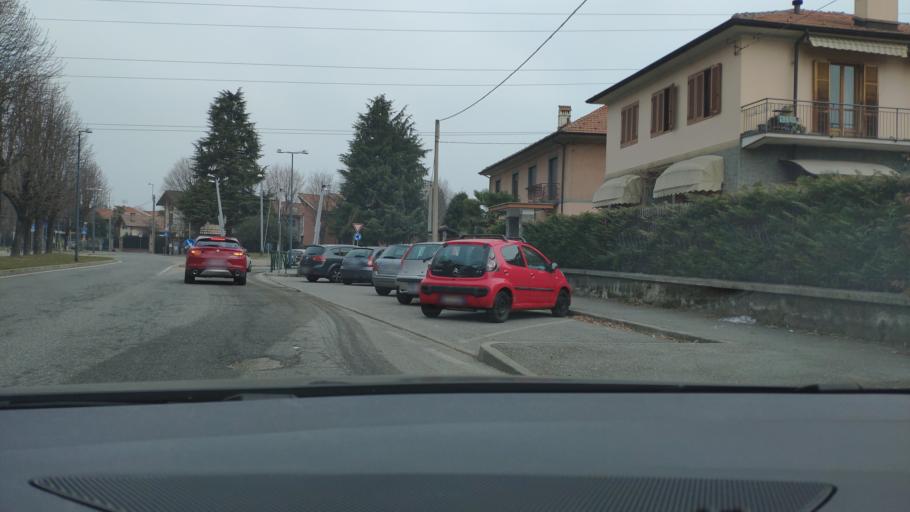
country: IT
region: Piedmont
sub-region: Provincia di Torino
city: Pianezza
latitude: 45.1087
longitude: 7.5463
